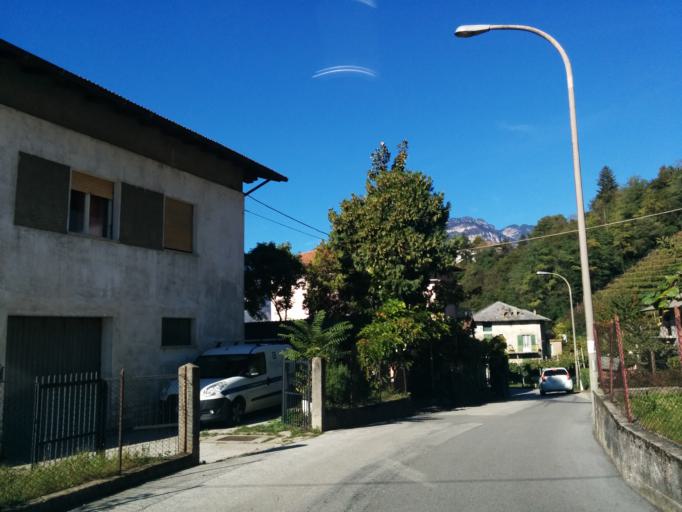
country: IT
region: Trentino-Alto Adige
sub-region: Provincia di Trento
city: San Michele All'Adige
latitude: 46.1748
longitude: 11.1245
